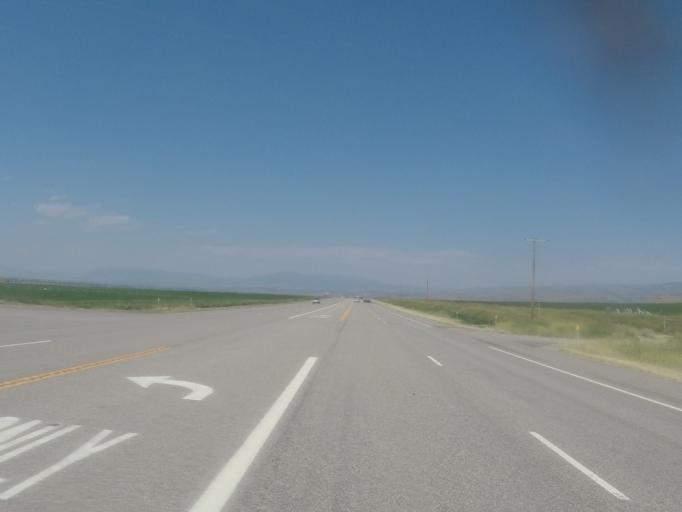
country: US
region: Montana
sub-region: Broadwater County
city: Townsend
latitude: 46.1072
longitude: -111.5109
